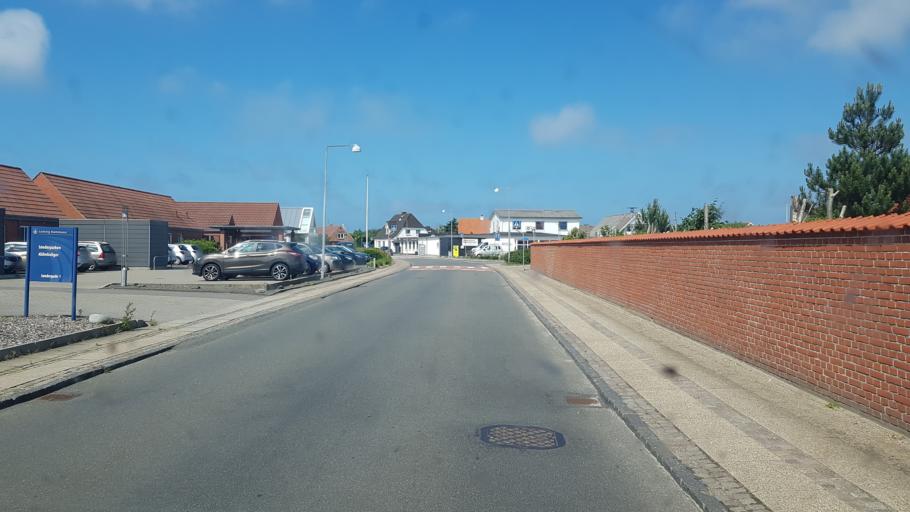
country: DK
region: Central Jutland
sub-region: Lemvig Kommune
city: Harboore
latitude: 56.6203
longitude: 8.1855
